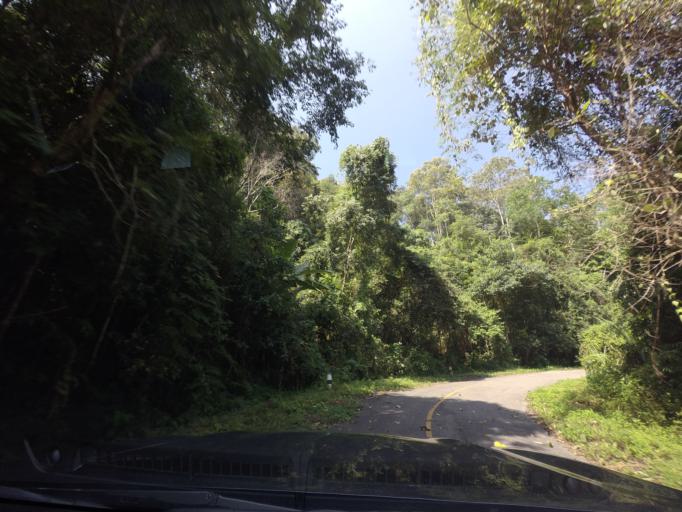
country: TH
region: Loei
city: Na Haeo
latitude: 17.5698
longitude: 100.9653
